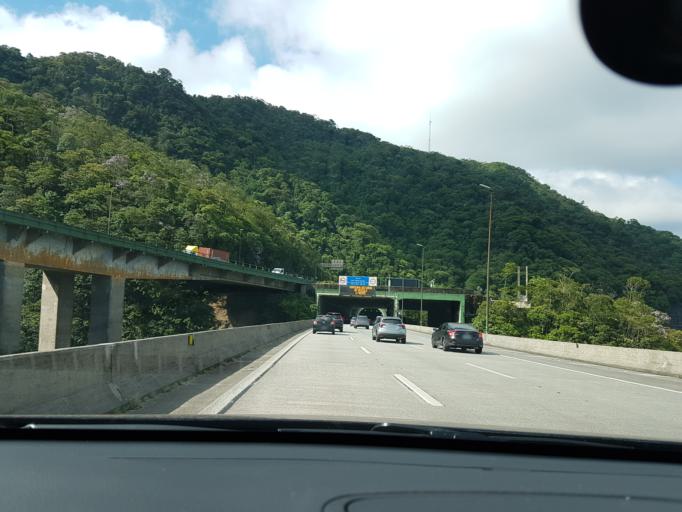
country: BR
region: Sao Paulo
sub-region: Cubatao
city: Cubatao
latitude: -23.9201
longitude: -46.5312
